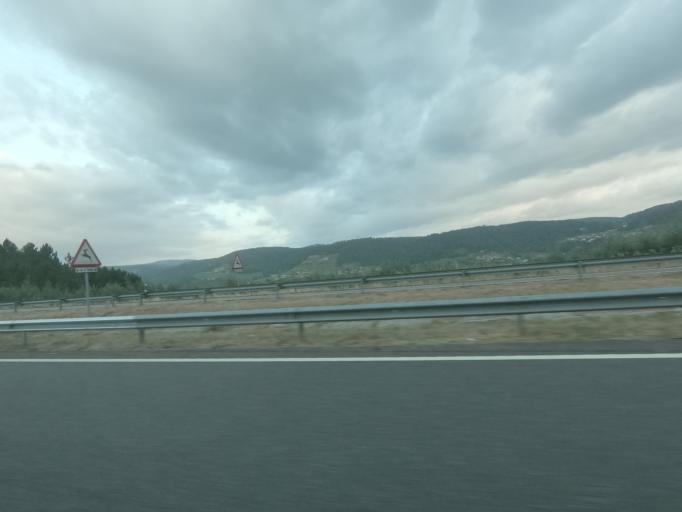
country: ES
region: Galicia
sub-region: Provincia de Ourense
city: Punxin
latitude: 42.3349
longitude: -8.0284
